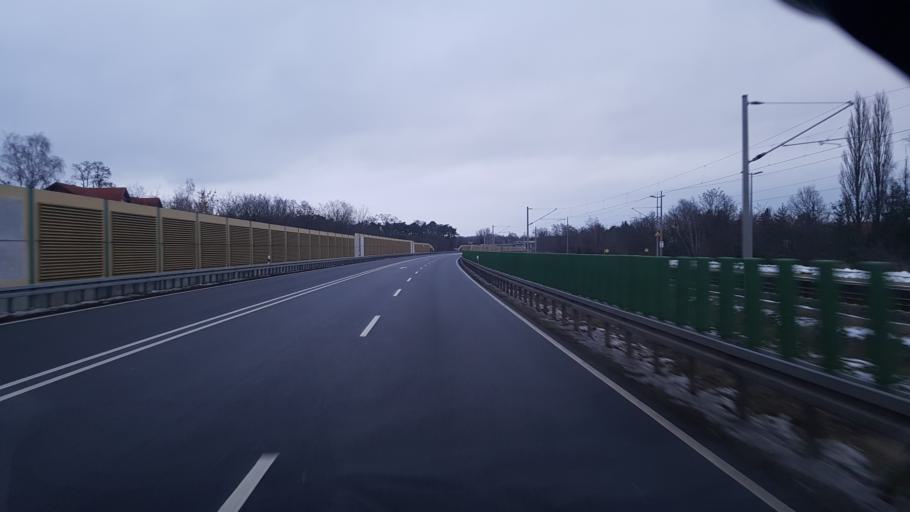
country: DE
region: Brandenburg
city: Brieskow-Finkenheerd
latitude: 52.2494
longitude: 14.5695
